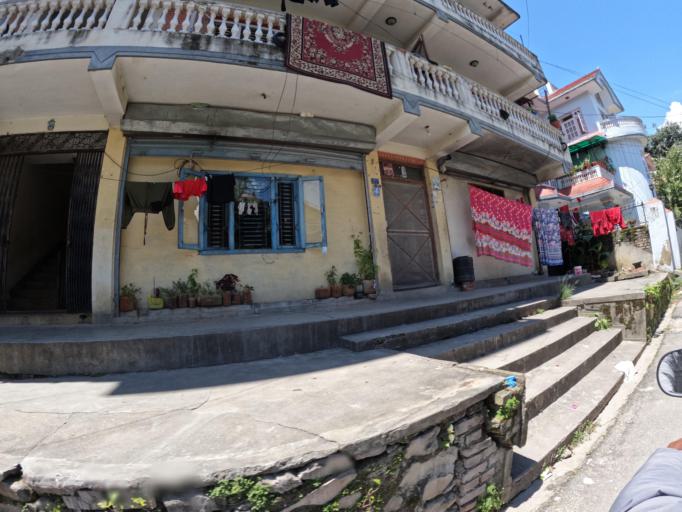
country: NP
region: Central Region
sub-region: Bagmati Zone
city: Kathmandu
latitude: 27.7423
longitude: 85.3257
